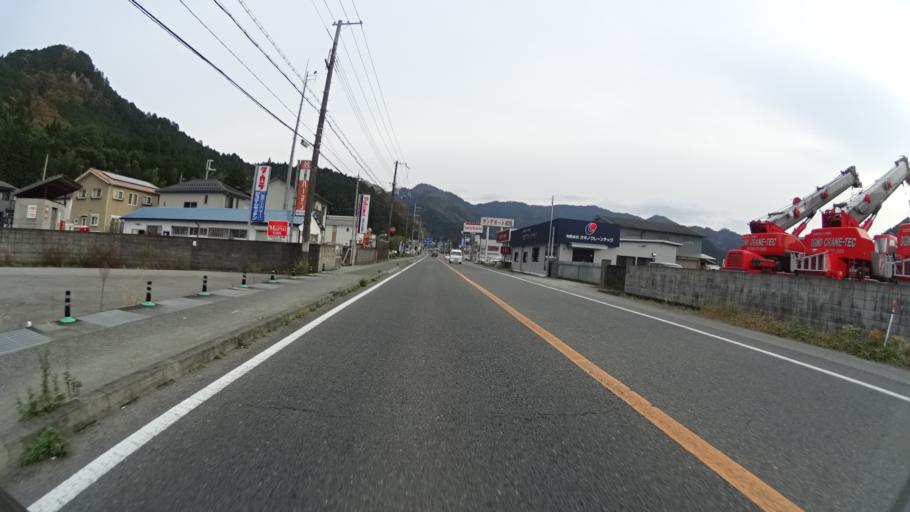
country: JP
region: Hyogo
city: Sasayama
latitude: 35.1211
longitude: 135.0866
